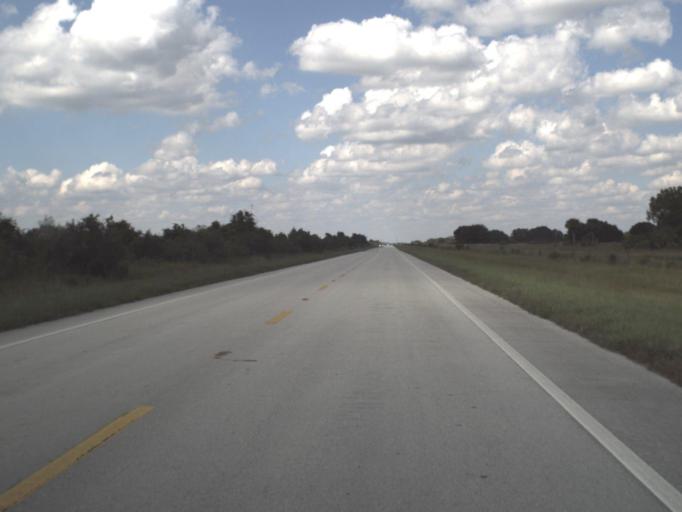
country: US
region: Florida
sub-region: Highlands County
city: Lake Placid
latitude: 27.4135
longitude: -81.1909
